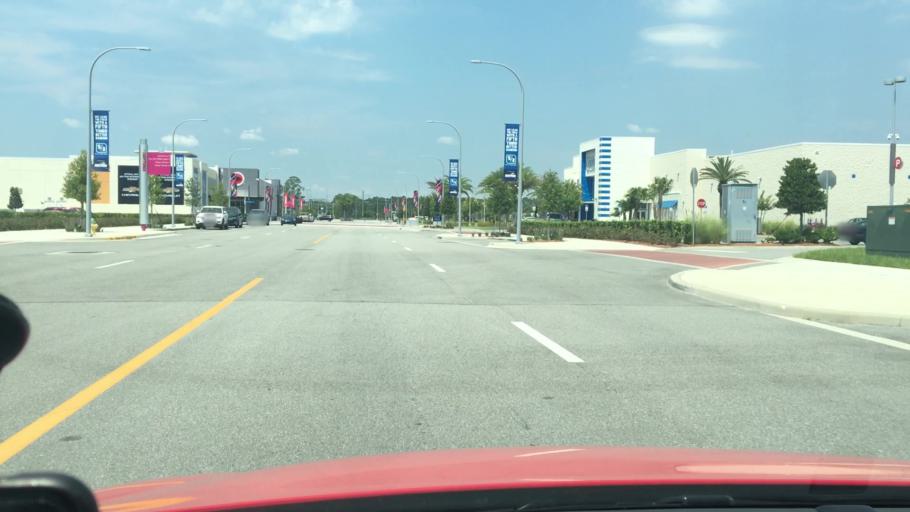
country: US
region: Florida
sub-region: Volusia County
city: Daytona Beach
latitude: 29.1960
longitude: -81.0713
